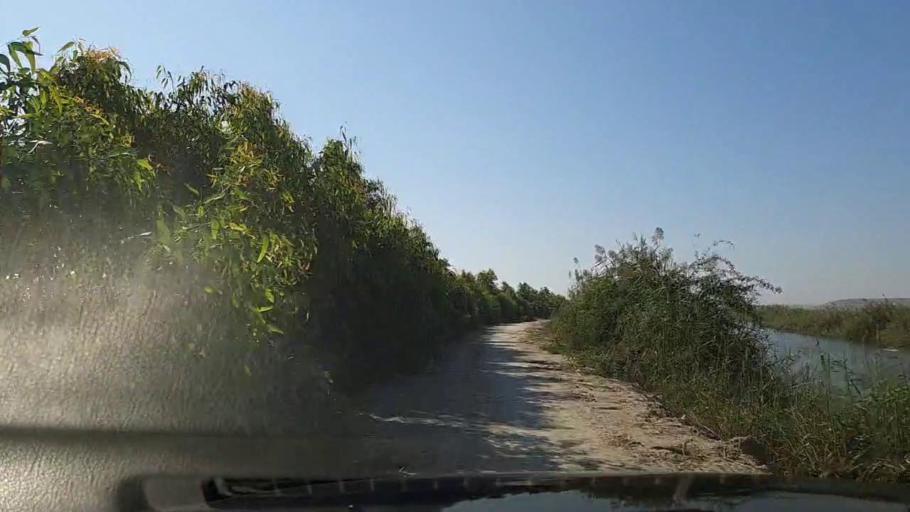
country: PK
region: Sindh
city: Thatta
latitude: 24.6941
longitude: 67.8954
